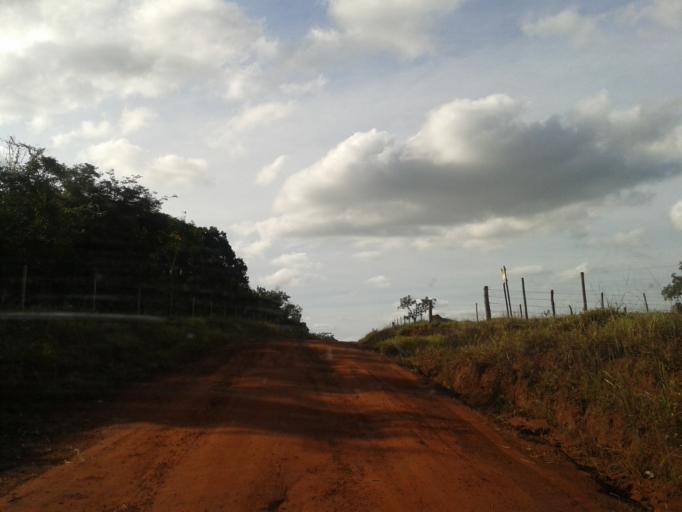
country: BR
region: Minas Gerais
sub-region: Campina Verde
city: Campina Verde
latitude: -19.4237
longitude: -49.7430
